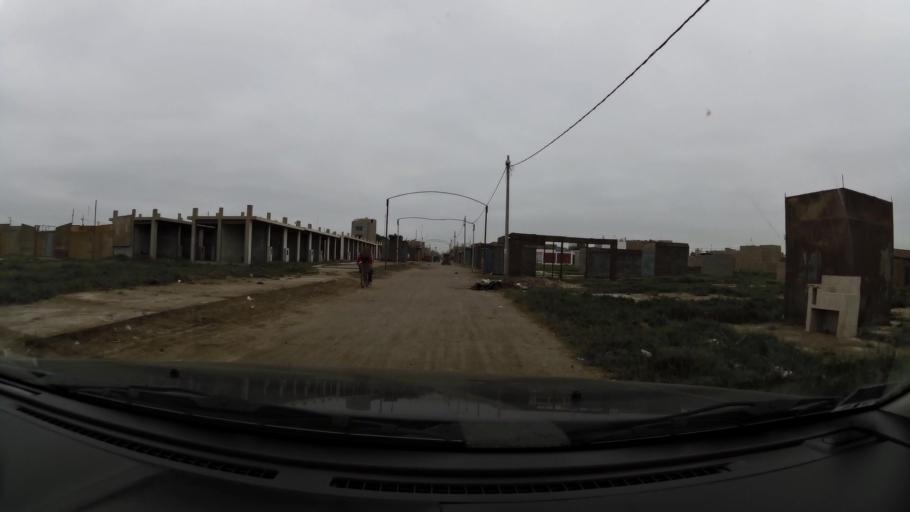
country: PE
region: Ica
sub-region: Provincia de Pisco
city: Pisco
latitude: -13.7144
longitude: -76.2114
